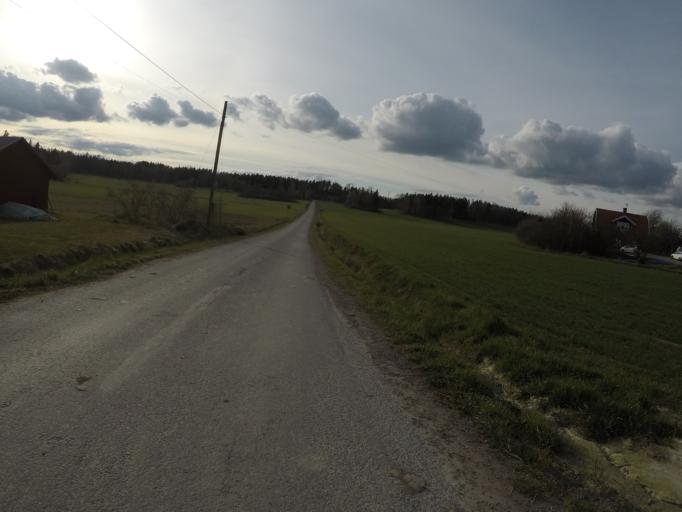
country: SE
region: Soedermanland
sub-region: Eskilstuna Kommun
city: Torshalla
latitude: 59.4310
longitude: 16.5181
